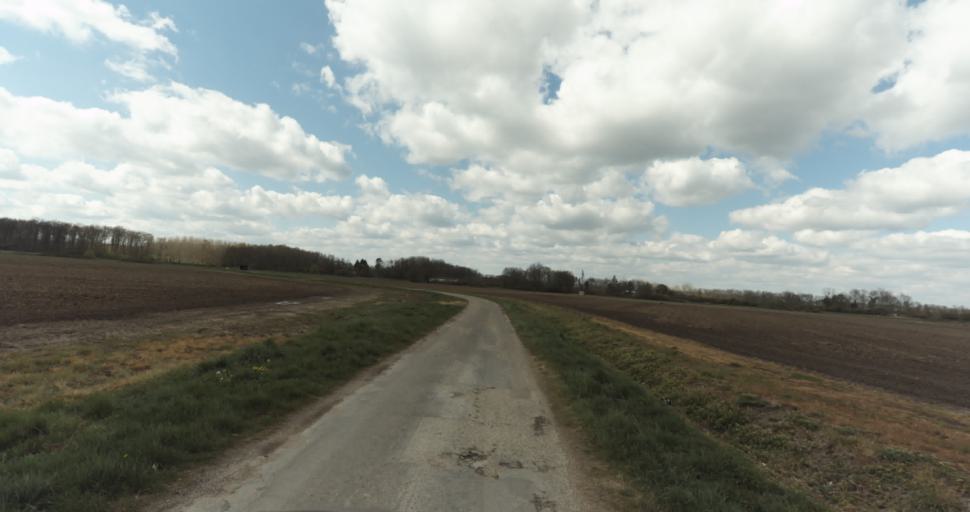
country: FR
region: Bourgogne
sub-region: Departement de la Cote-d'Or
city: Auxonne
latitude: 47.1800
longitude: 5.3777
